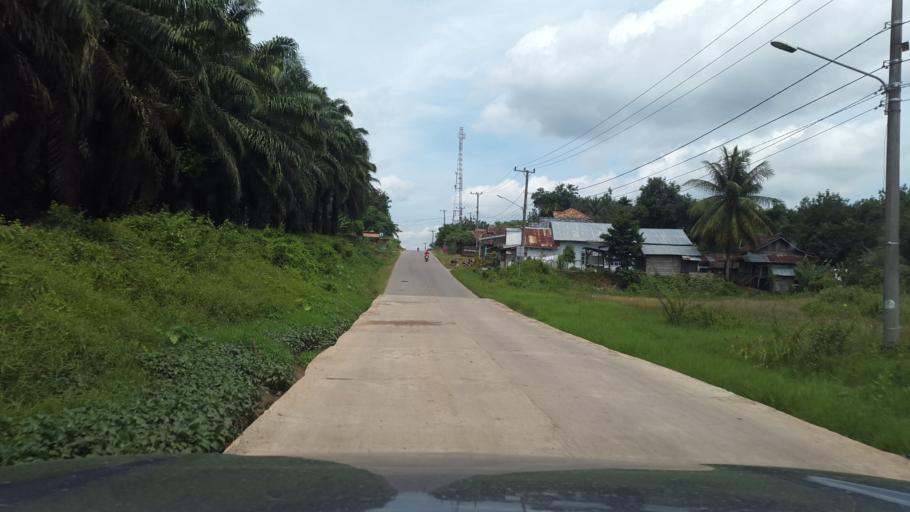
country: ID
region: South Sumatra
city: Gunungmegang Dalam
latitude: -3.3338
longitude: 103.9088
